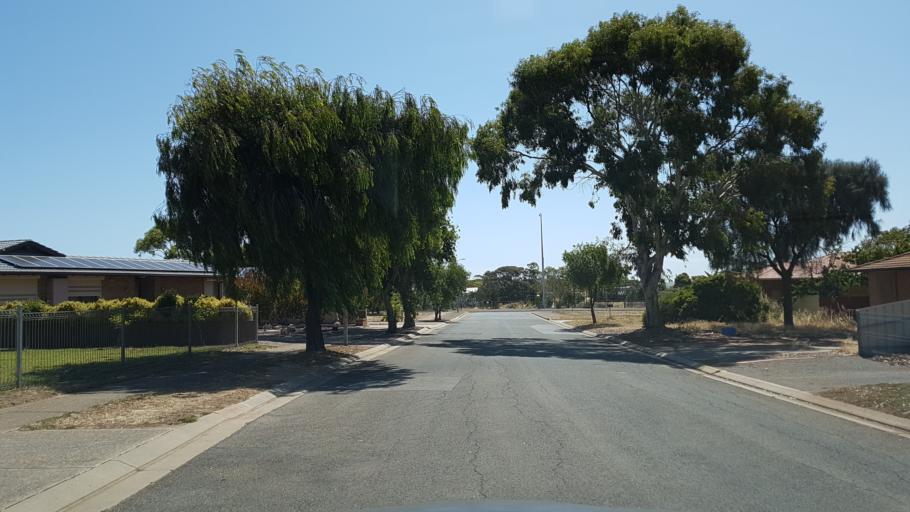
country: AU
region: South Australia
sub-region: Onkaparinga
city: Morphett Vale
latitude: -35.1100
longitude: 138.5108
